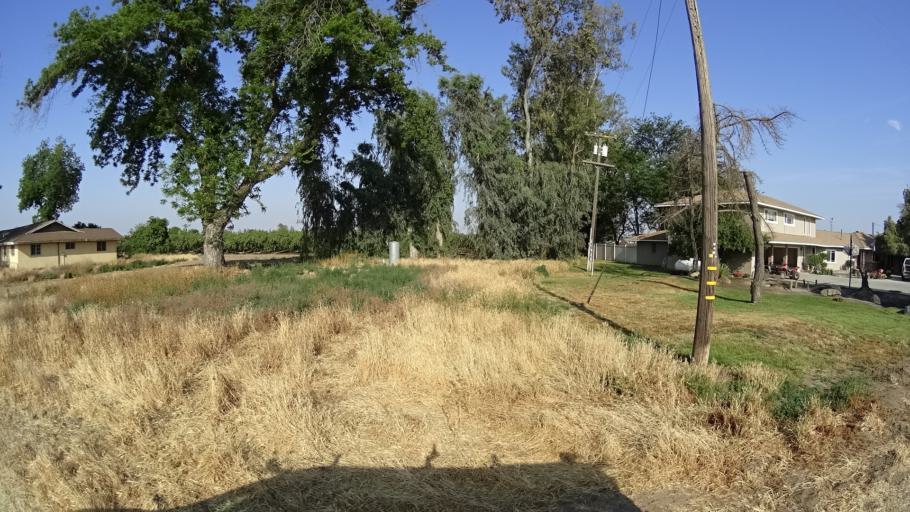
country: US
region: California
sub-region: Fresno County
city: Riverdale
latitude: 36.3741
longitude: -119.8431
